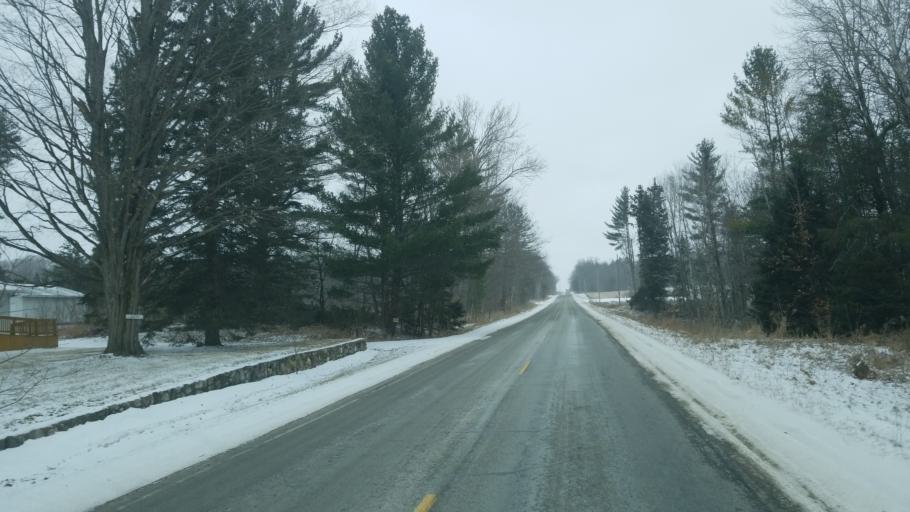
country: US
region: Michigan
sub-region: Osceola County
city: Evart
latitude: 44.0139
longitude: -85.2464
